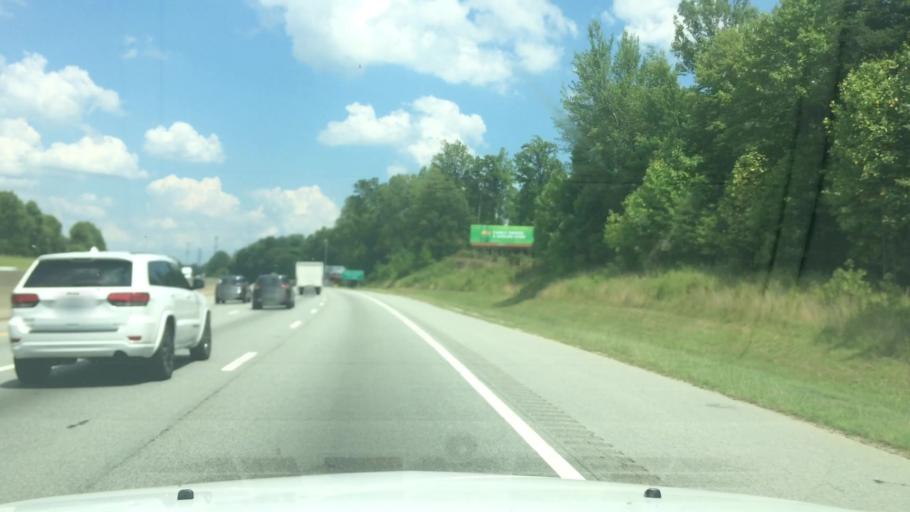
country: US
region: North Carolina
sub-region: Guilford County
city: Greensboro
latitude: 36.0468
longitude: -79.7524
